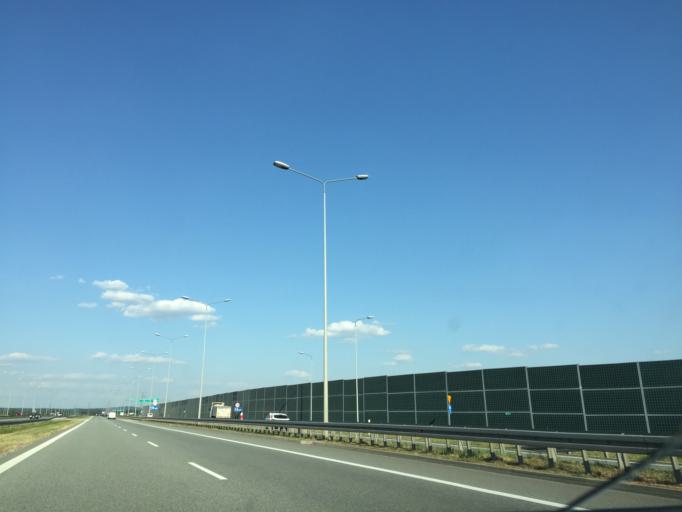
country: PL
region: Swietokrzyskie
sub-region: Powiat kielecki
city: Kostomloty Drugie
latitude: 50.9070
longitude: 20.5705
